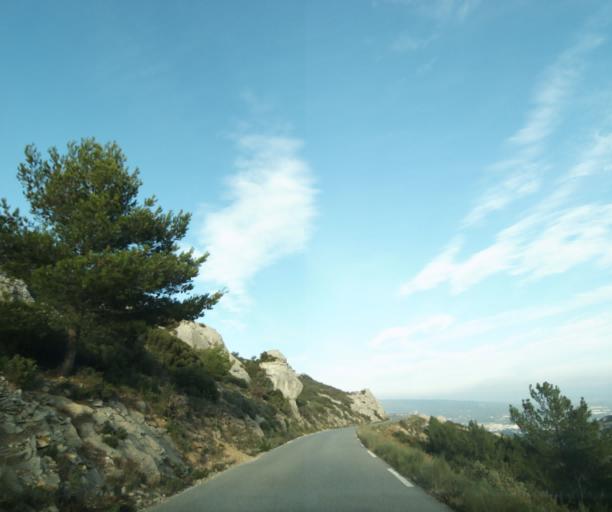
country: FR
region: Provence-Alpes-Cote d'Azur
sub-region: Departement des Bouches-du-Rhone
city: Cassis
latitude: 43.1882
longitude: 5.5621
